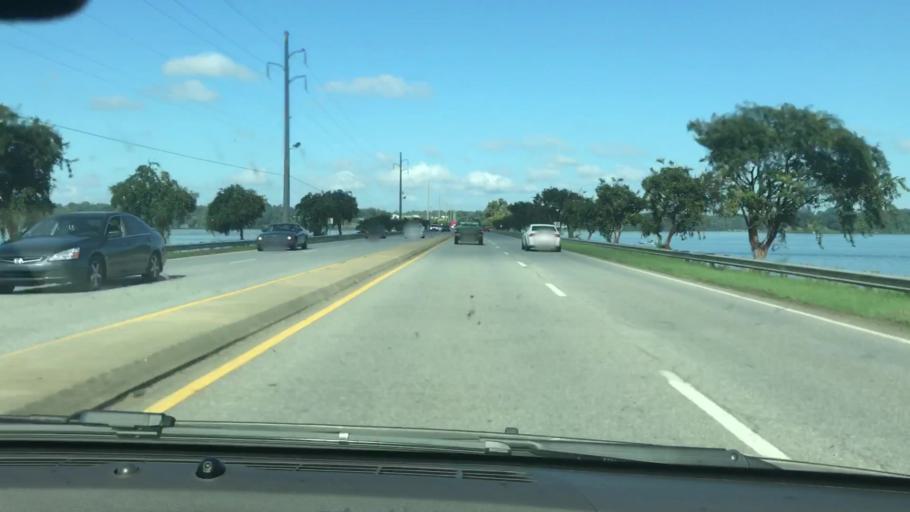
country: US
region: Georgia
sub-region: Quitman County
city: Georgetown
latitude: 31.8888
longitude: -85.1143
